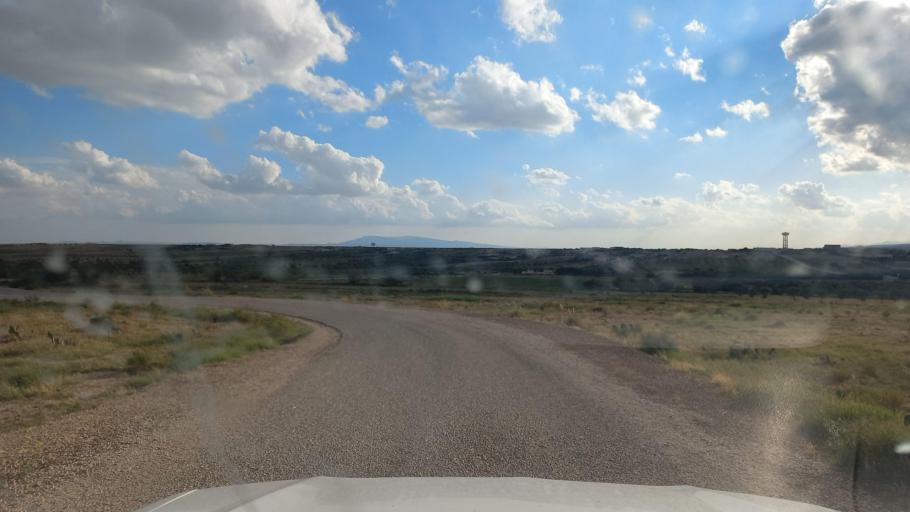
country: TN
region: Al Qasrayn
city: Sbiba
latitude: 35.3777
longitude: 9.0722
